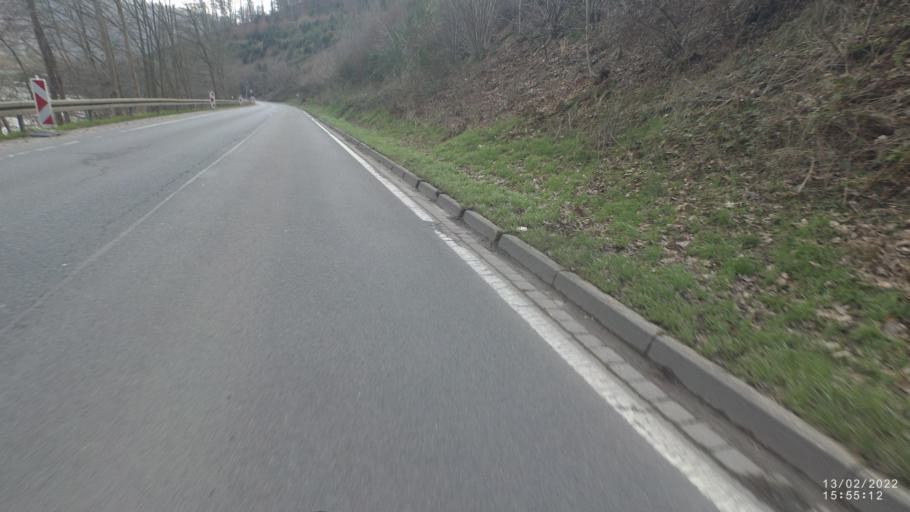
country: DE
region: North Rhine-Westphalia
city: Altena
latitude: 51.2783
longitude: 7.7030
